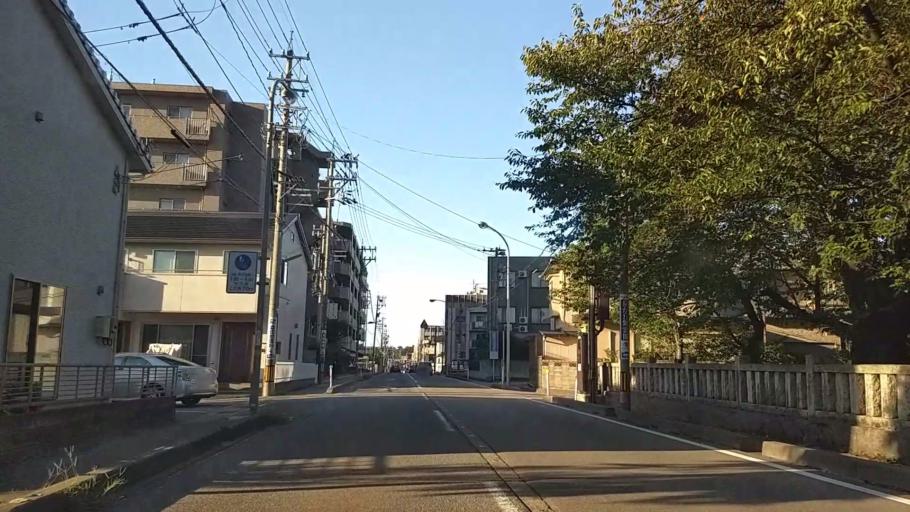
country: JP
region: Ishikawa
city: Nonoichi
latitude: 36.5447
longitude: 136.6489
